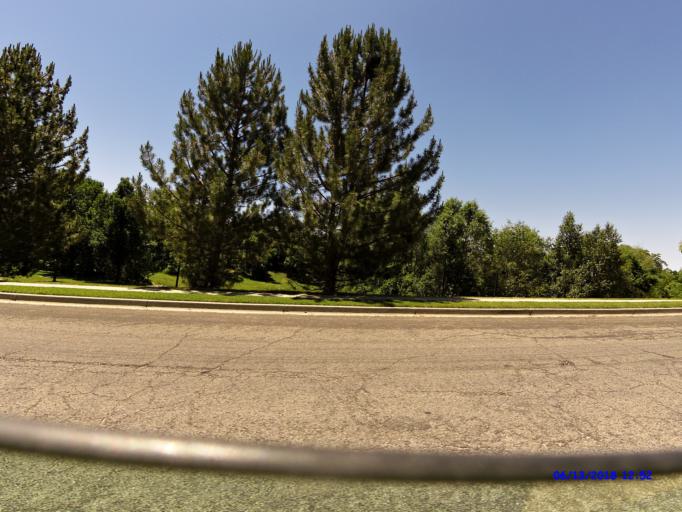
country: US
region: Utah
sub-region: Weber County
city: Ogden
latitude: 41.2087
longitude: -111.9590
